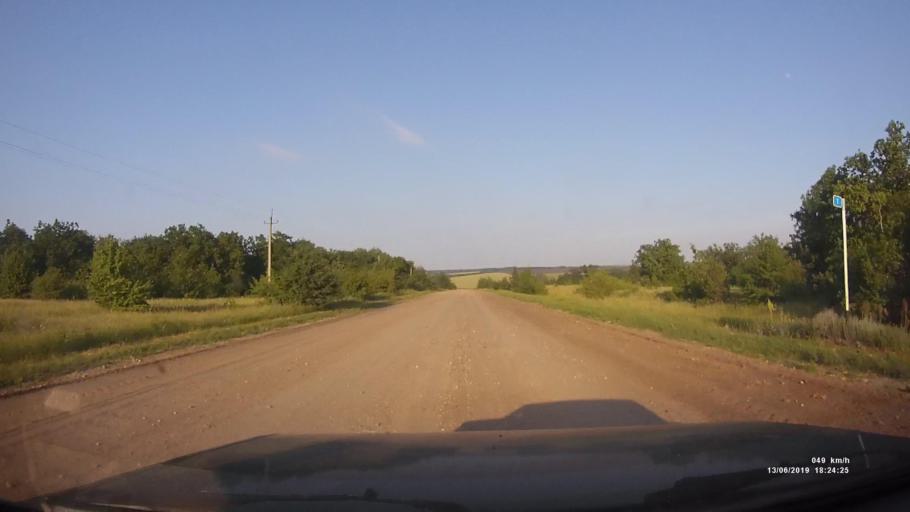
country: RU
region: Rostov
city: Kazanskaya
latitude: 49.8519
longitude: 41.2893
